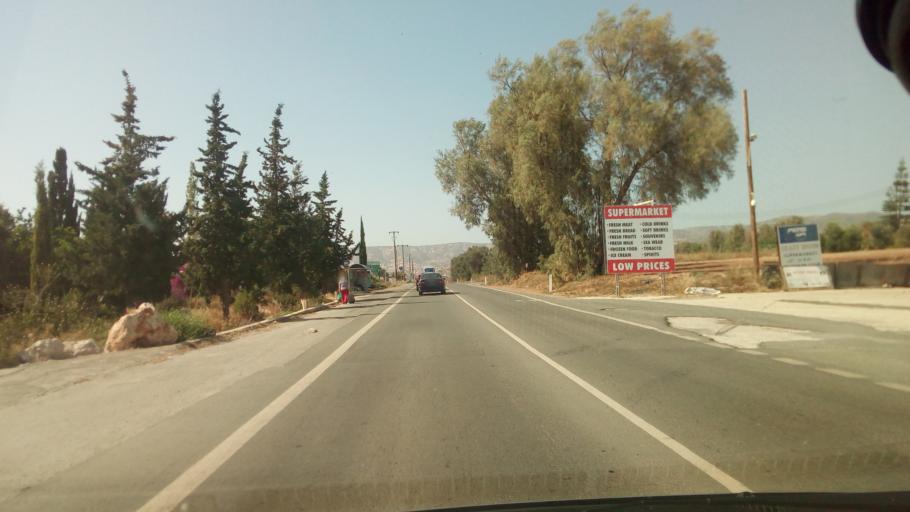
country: CY
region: Pafos
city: Kissonerga
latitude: 34.8264
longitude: 32.3923
